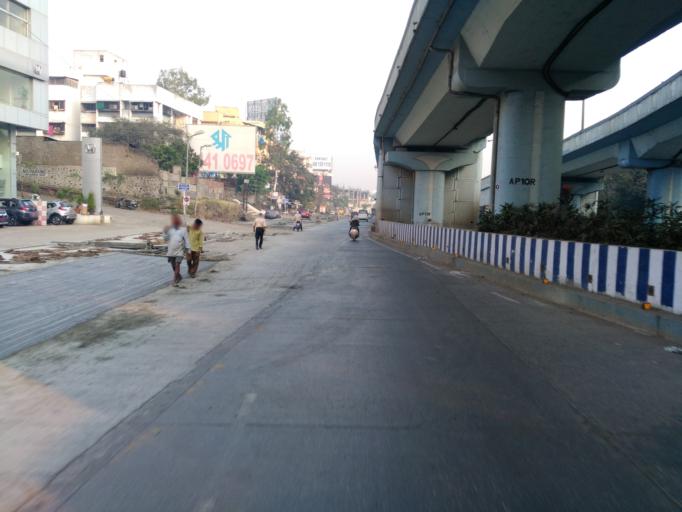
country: IN
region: Maharashtra
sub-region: Pune Division
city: Pune
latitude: 18.4707
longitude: 73.8570
